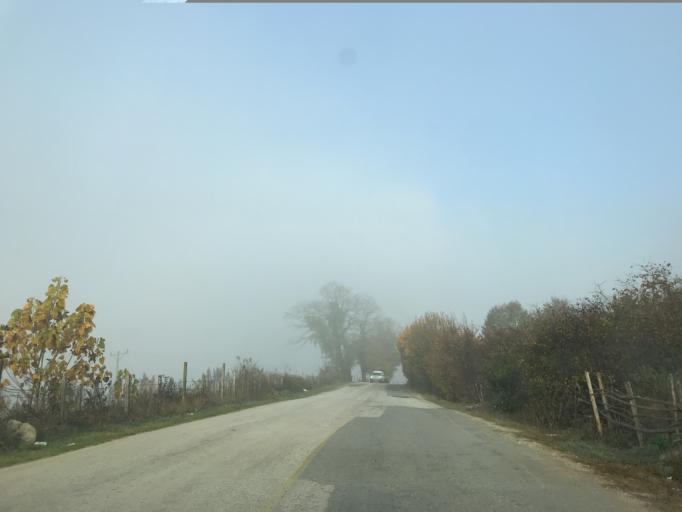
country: TR
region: Duzce
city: Cumayeri
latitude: 40.8971
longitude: 30.9526
